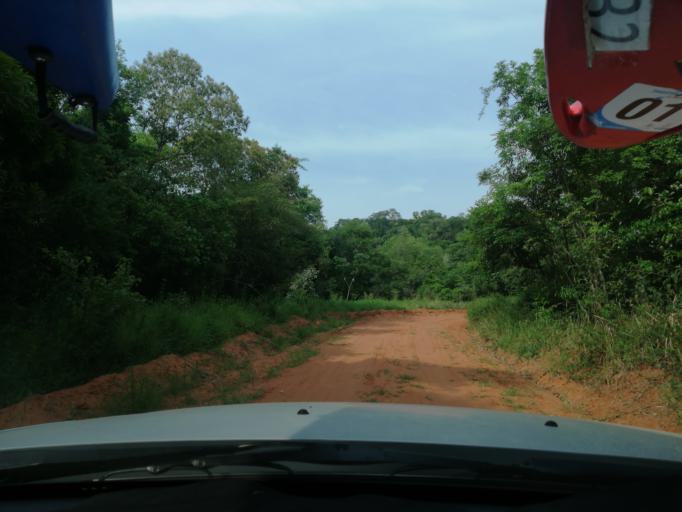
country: AR
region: Misiones
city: Santa Ana
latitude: -27.3064
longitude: -55.5822
